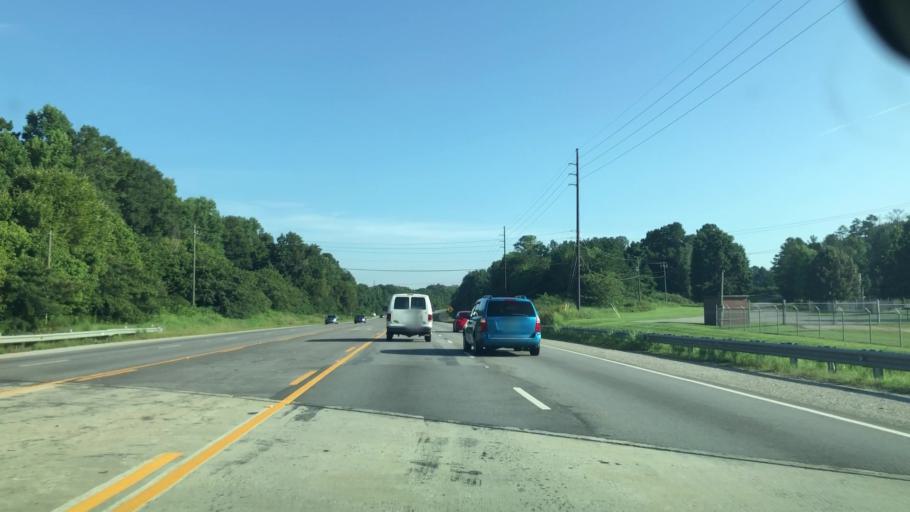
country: US
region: Alabama
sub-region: Calhoun County
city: Bynum
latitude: 33.6034
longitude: -85.9272
